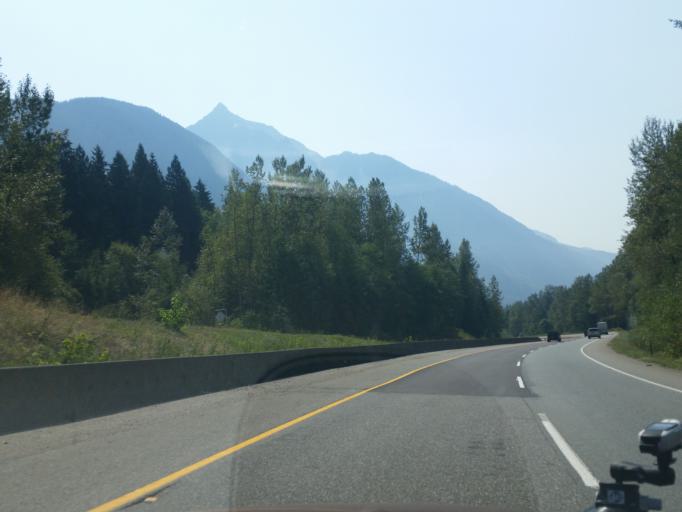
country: CA
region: British Columbia
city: Agassiz
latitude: 49.2405
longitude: -121.6786
